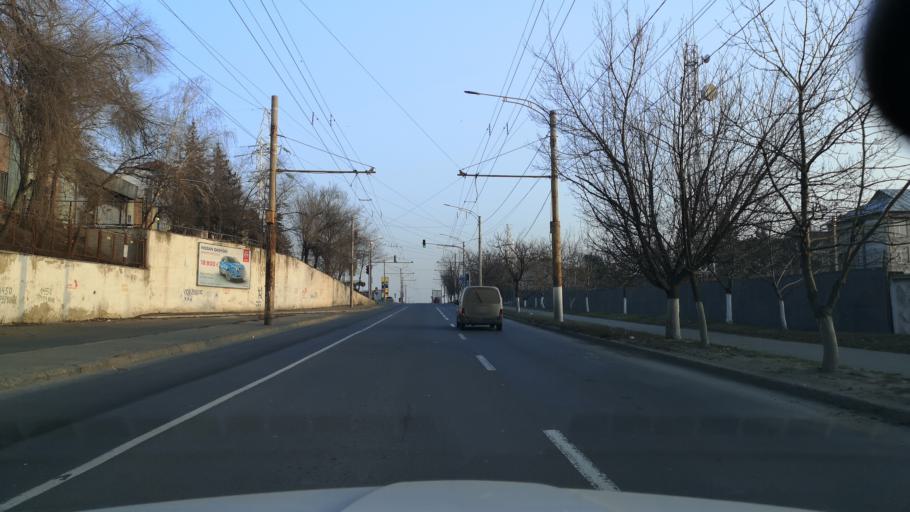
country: MD
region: Chisinau
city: Chisinau
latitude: 47.0467
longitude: 28.8285
